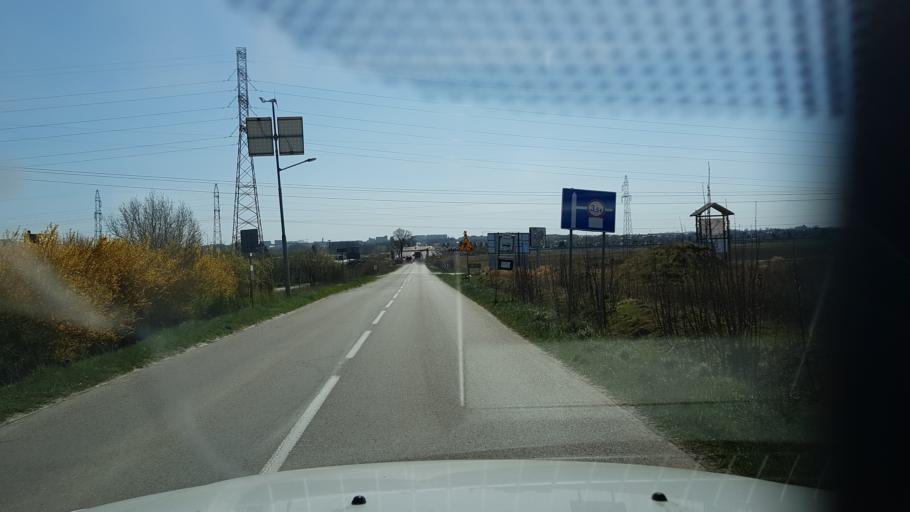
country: PL
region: West Pomeranian Voivodeship
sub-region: Koszalin
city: Koszalin
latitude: 54.2360
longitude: 16.1775
